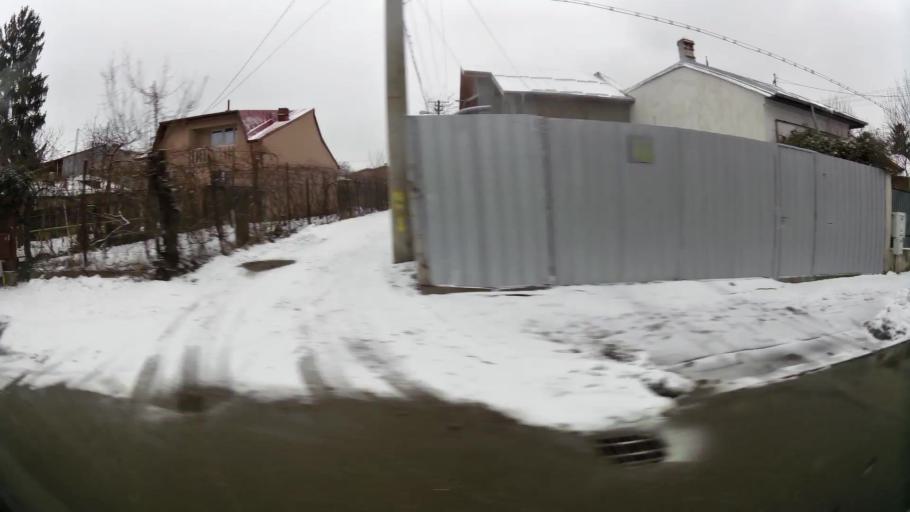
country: RO
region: Prahova
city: Ploiesti
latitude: 44.9325
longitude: 26.0424
